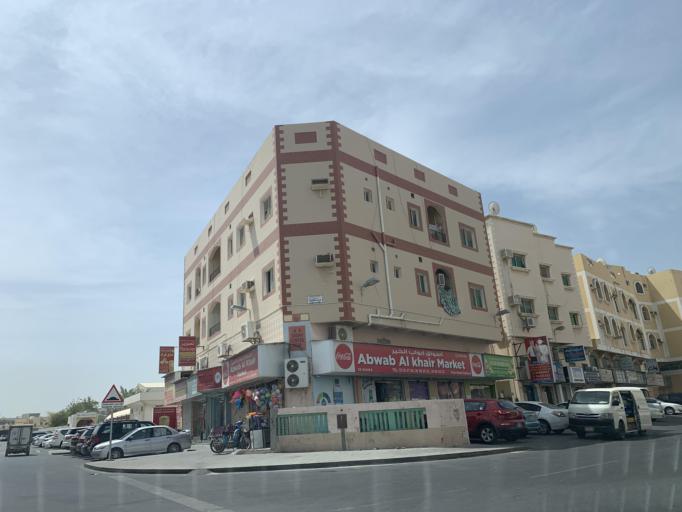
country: BH
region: Northern
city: Ar Rifa'
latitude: 26.1429
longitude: 50.5646
